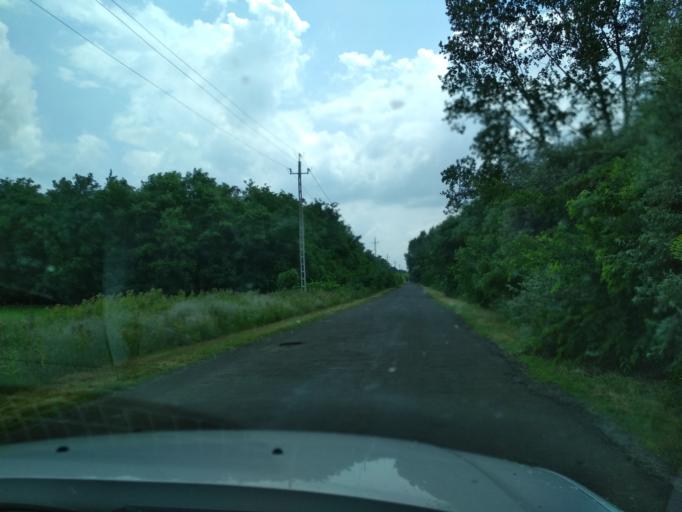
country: HU
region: Pest
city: Nagykata
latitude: 47.3878
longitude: 19.7564
